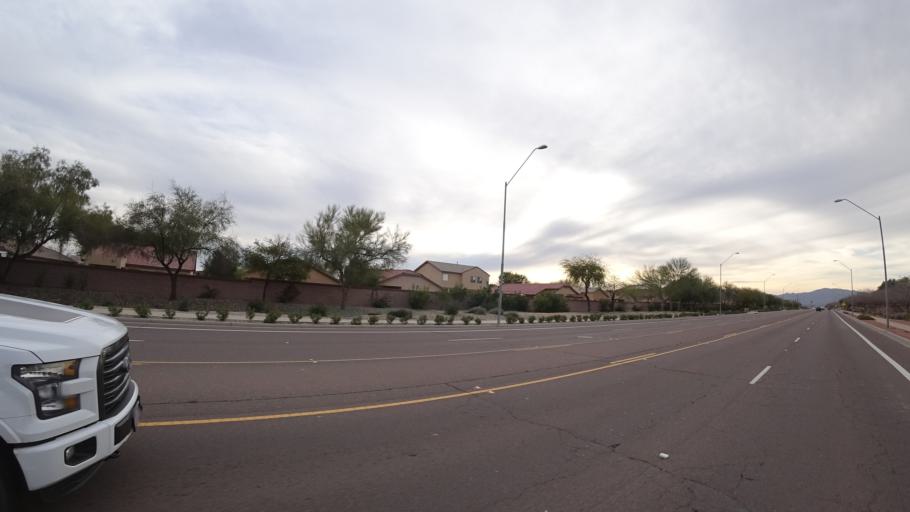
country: US
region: Arizona
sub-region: Maricopa County
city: Surprise
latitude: 33.6243
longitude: -112.4036
